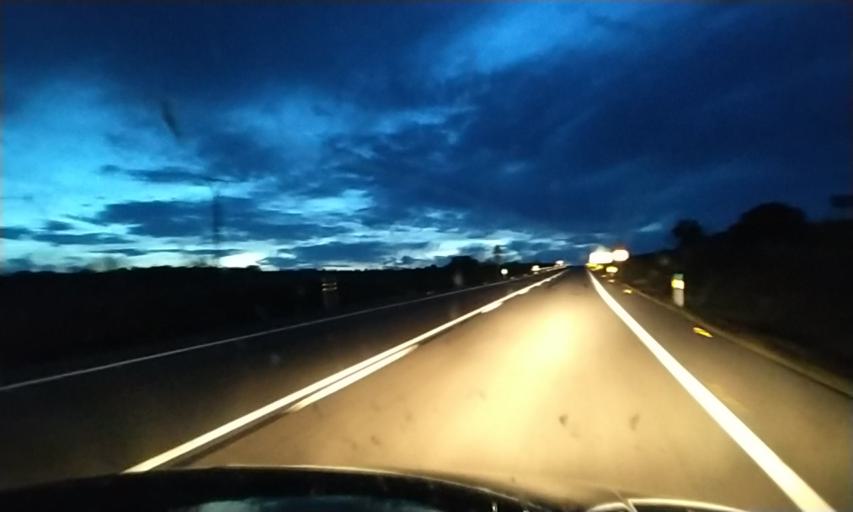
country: ES
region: Extremadura
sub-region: Provincia de Caceres
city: Carcaboso
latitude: 39.9806
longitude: -6.1644
